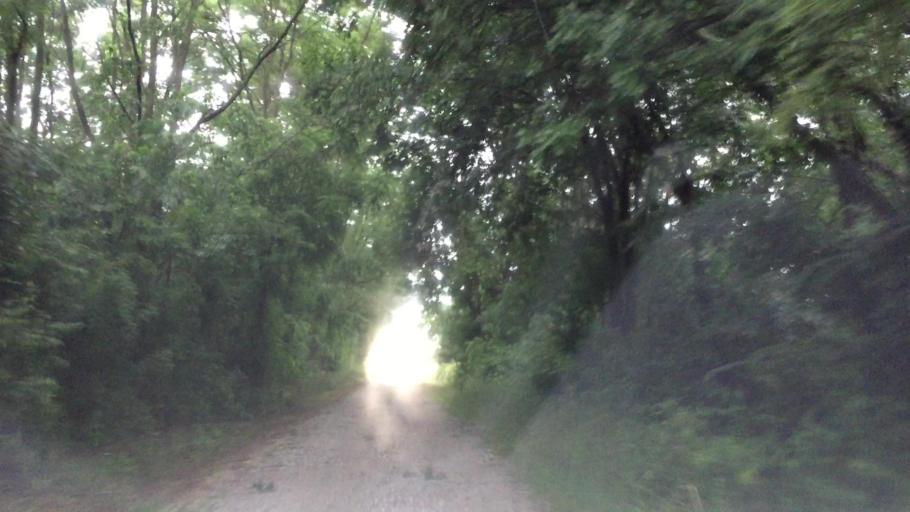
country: US
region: Illinois
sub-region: Hancock County
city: Nauvoo
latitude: 40.5500
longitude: -91.3513
